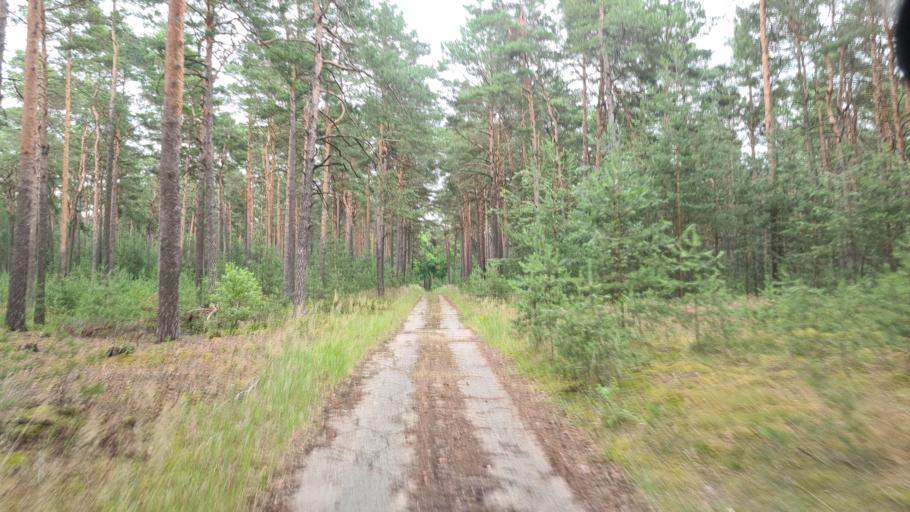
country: DE
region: Brandenburg
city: Crinitz
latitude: 51.7162
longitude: 13.7411
